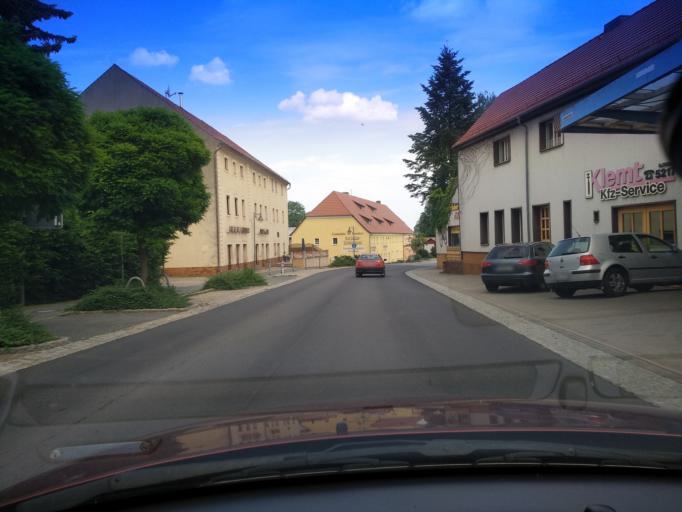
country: DE
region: Saxony
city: Kodersdorf
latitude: 51.2304
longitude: 14.8931
